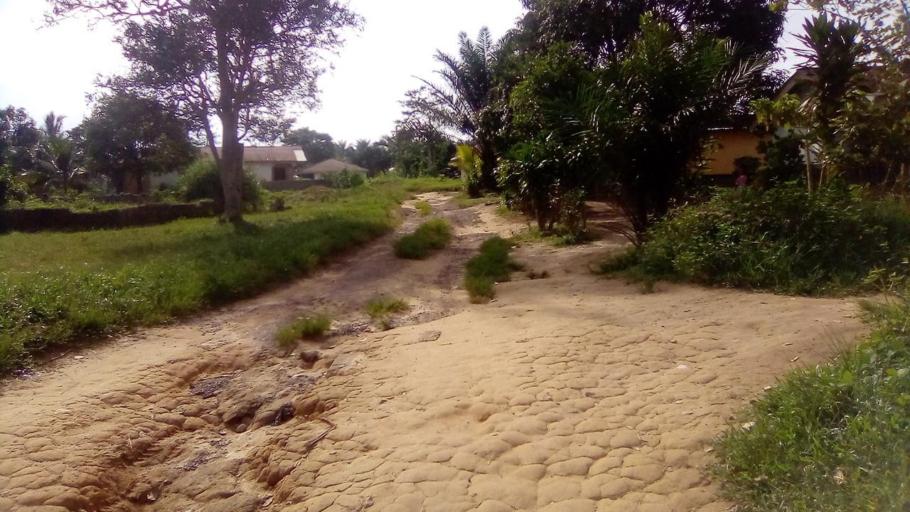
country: SL
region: Southern Province
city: Pujehun
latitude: 7.3640
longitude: -11.7227
